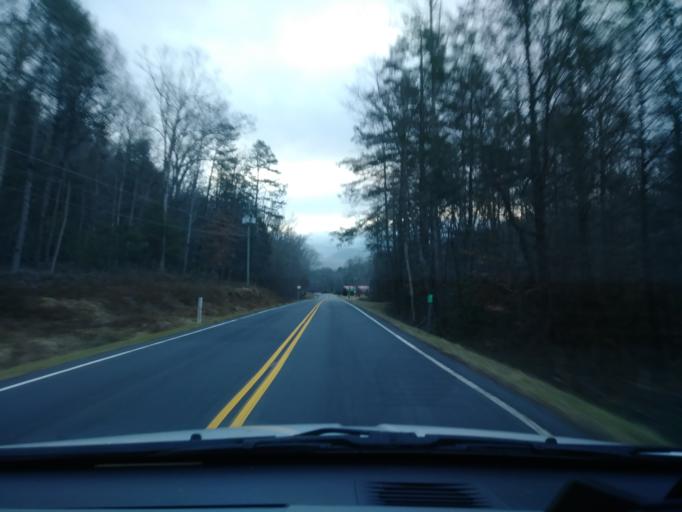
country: US
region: Tennessee
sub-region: Unicoi County
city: Unicoi
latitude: 36.1826
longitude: -82.3251
